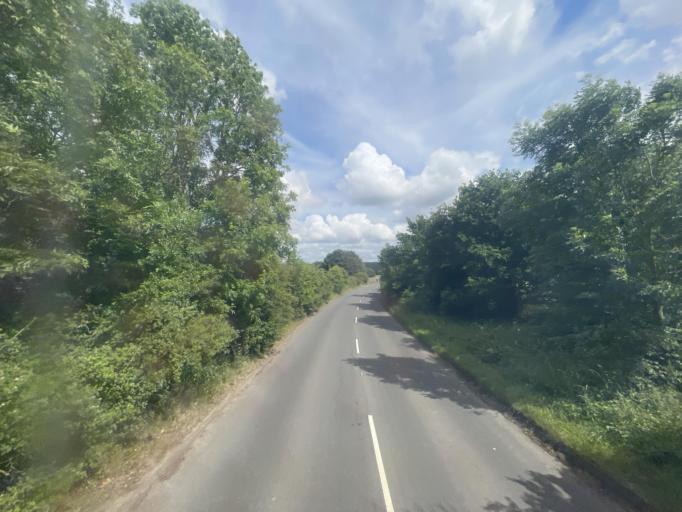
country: GB
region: England
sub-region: Kent
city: Westerham
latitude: 51.2763
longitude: 0.0830
